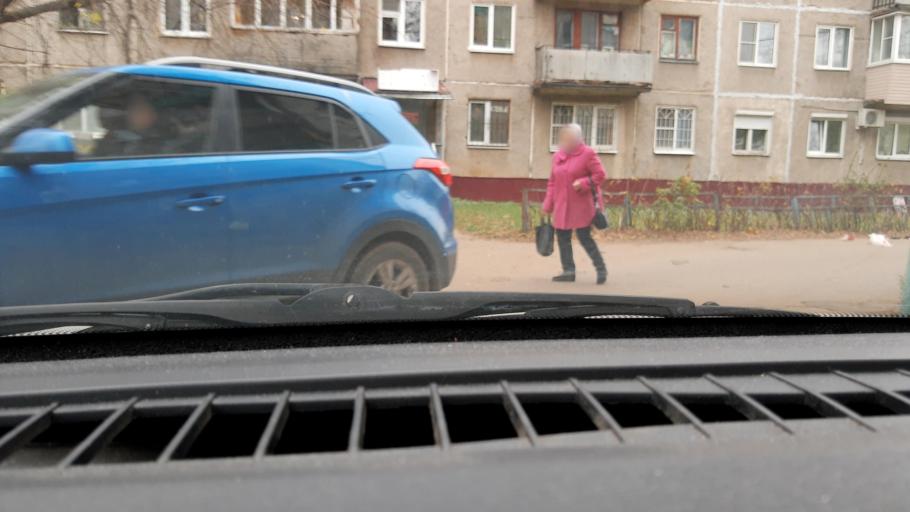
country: RU
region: Nizjnij Novgorod
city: Burevestnik
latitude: 56.2254
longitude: 43.8626
